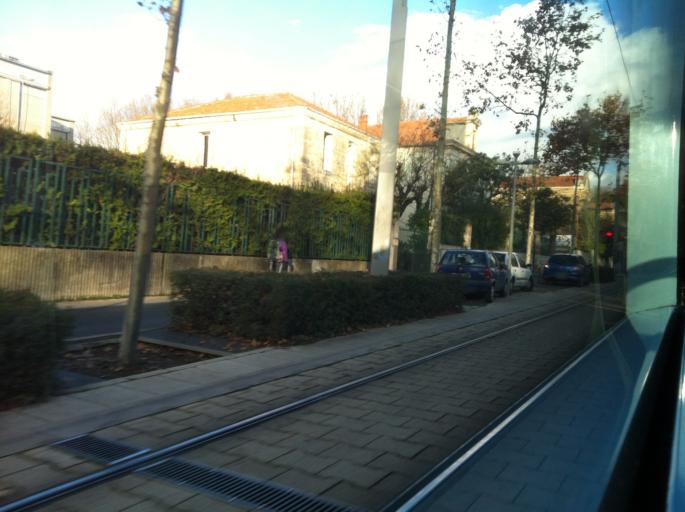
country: FR
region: Languedoc-Roussillon
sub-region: Departement de l'Herault
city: Montpellier
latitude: 43.6210
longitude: 3.8687
